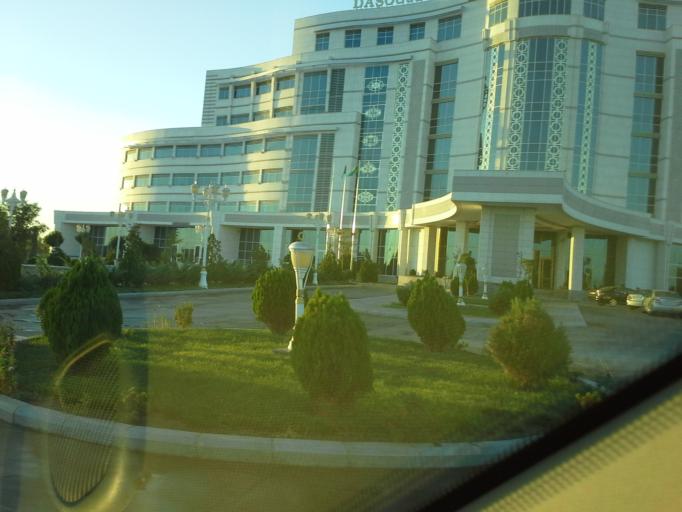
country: TM
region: Dasoguz
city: Dasoguz
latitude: 41.8239
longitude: 59.9293
